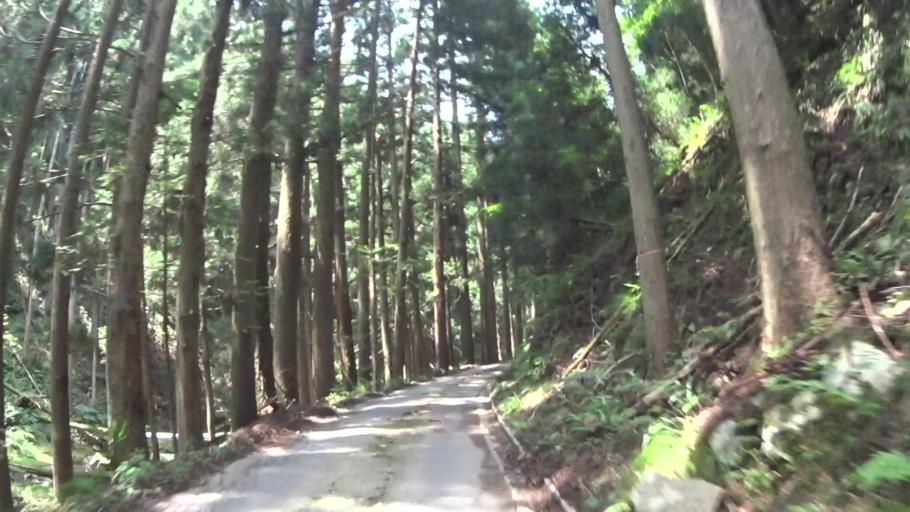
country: JP
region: Kyoto
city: Ayabe
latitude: 35.3014
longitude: 135.3984
